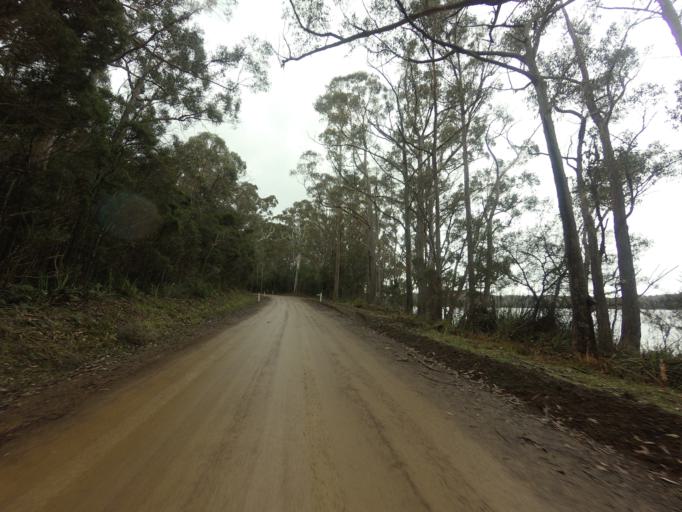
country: AU
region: Tasmania
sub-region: Huon Valley
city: Geeveston
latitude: -43.5309
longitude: 146.8947
